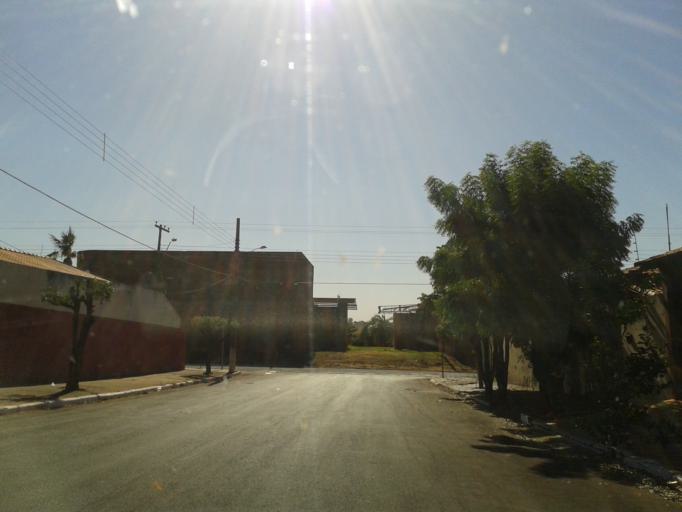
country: BR
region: Minas Gerais
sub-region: Santa Vitoria
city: Santa Vitoria
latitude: -18.8499
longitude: -50.1303
